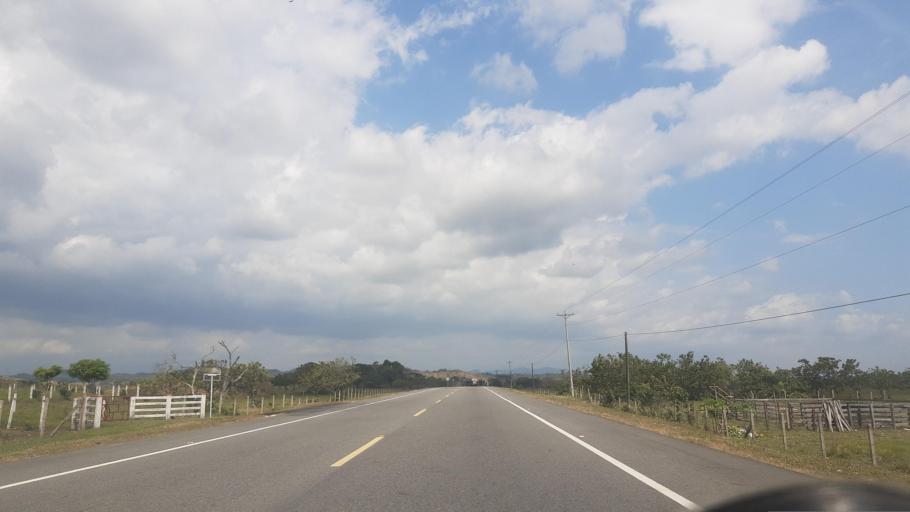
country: CO
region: Casanare
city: Tauramena
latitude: 4.9089
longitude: -72.6759
